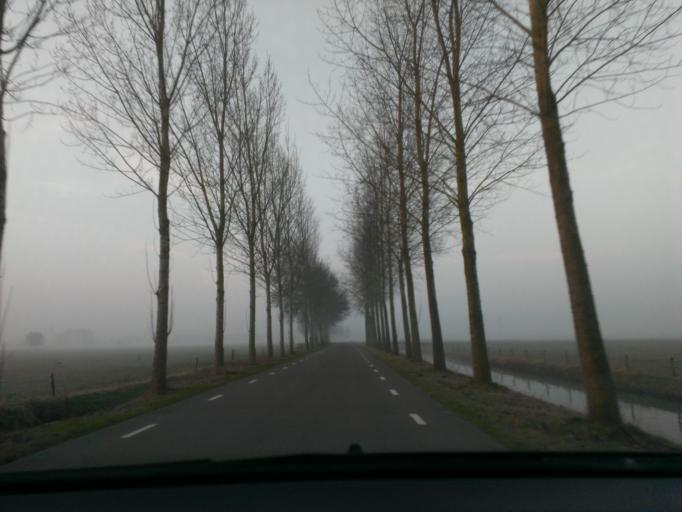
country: NL
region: Gelderland
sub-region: Gemeente Epe
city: Oene
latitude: 52.3197
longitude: 6.0486
